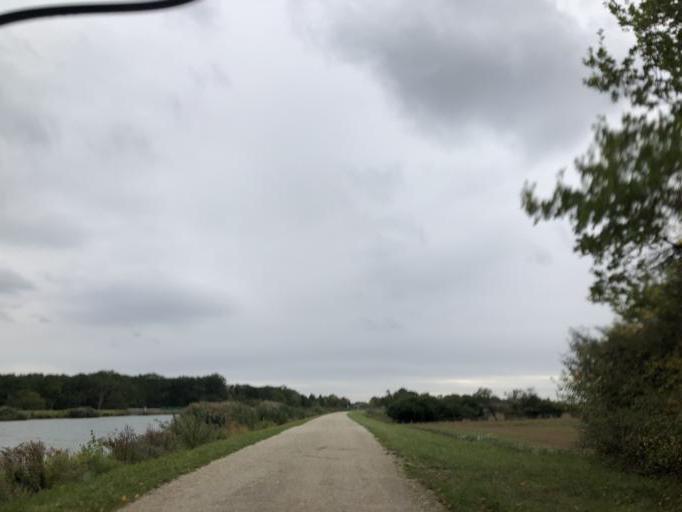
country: DE
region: Bavaria
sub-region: Regierungsbezirk Mittelfranken
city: Obermichelbach
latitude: 49.5415
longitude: 10.9688
